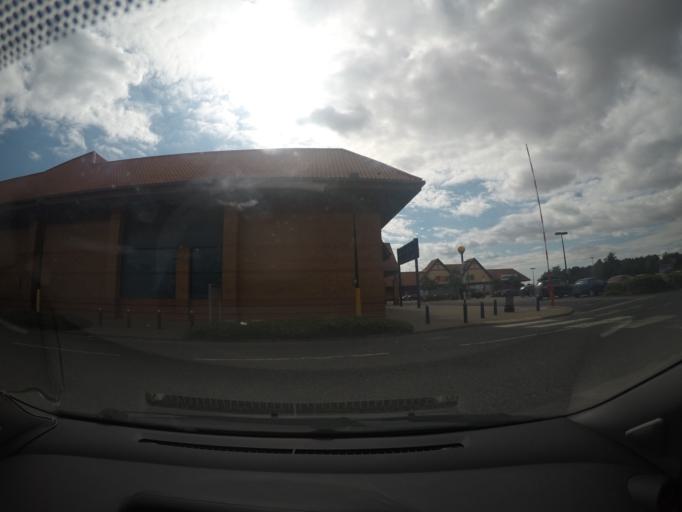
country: GB
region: England
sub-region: City of York
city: Skelton
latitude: 53.9906
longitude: -1.1094
